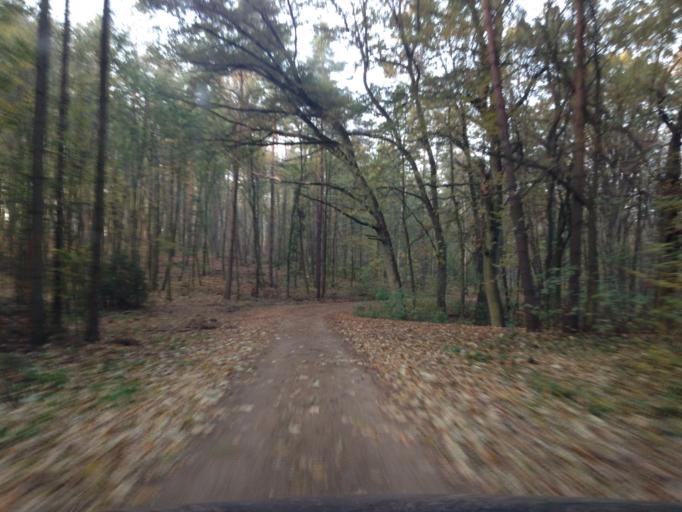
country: PL
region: Warmian-Masurian Voivodeship
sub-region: Powiat dzialdowski
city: Lidzbark
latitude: 53.2569
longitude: 19.7741
